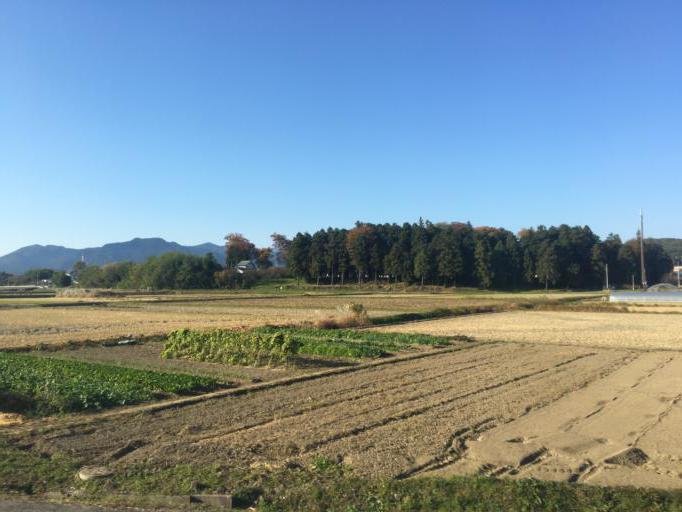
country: JP
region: Gunma
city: Fujioka
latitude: 36.2279
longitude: 139.0824
